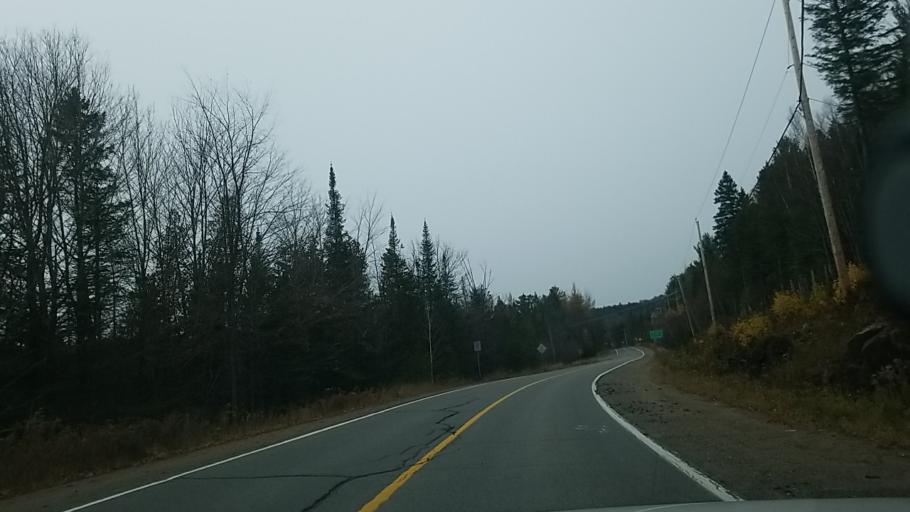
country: CA
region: Quebec
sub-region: Laurentides
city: Saint-Colomban
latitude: 45.7960
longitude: -74.1699
